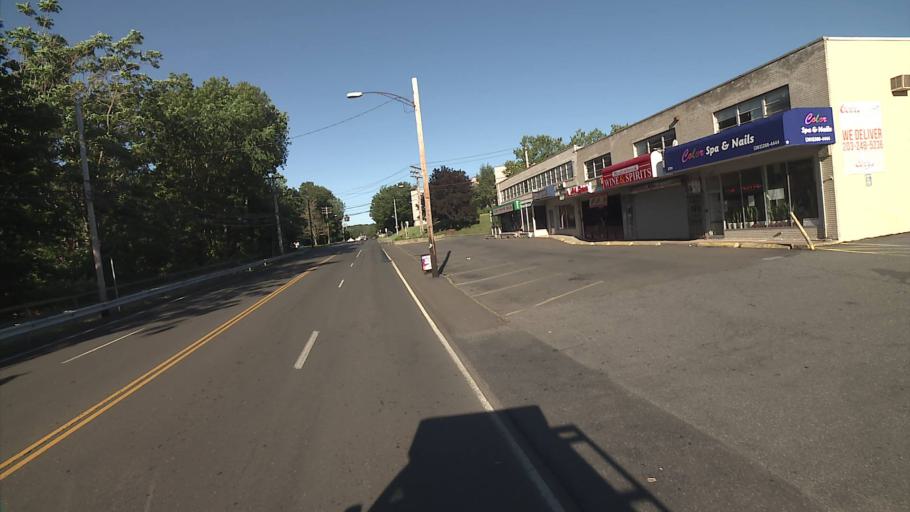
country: US
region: Connecticut
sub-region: New Haven County
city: Hamden
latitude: 41.3832
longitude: -72.9068
